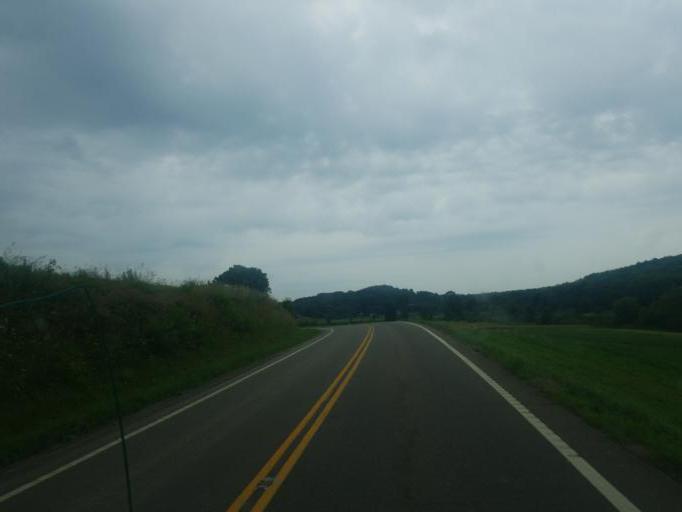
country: US
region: Ohio
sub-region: Stark County
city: Minerva
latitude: 40.7063
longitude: -81.0041
